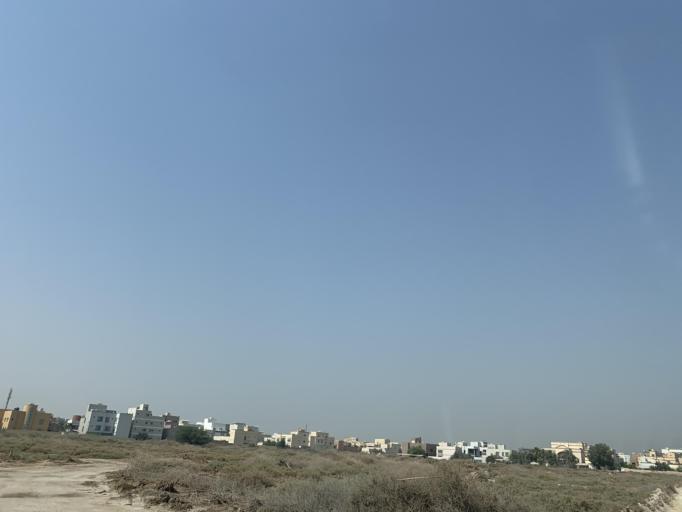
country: BH
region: Manama
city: Jidd Hafs
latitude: 26.2006
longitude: 50.5154
